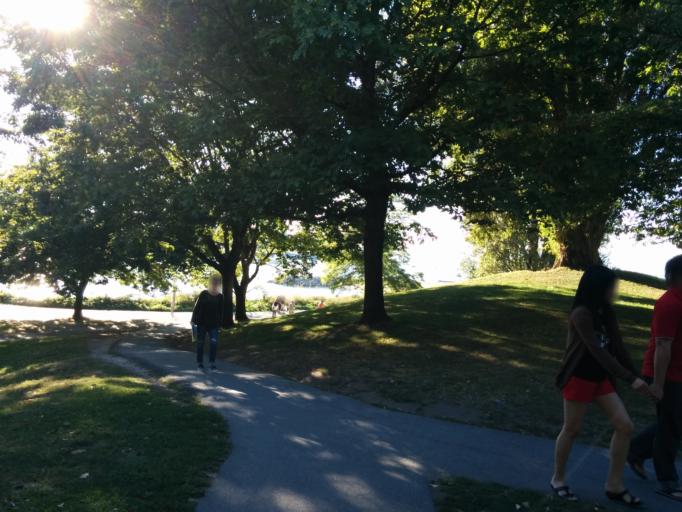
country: CA
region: British Columbia
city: West End
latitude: 49.2773
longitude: -123.1355
